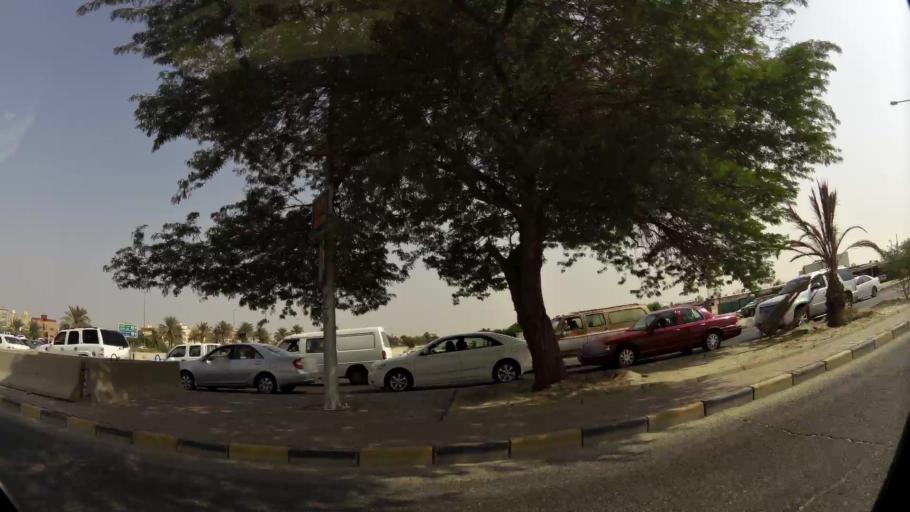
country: KW
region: Muhafazat al Jahra'
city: Al Jahra'
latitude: 29.3338
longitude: 47.6831
